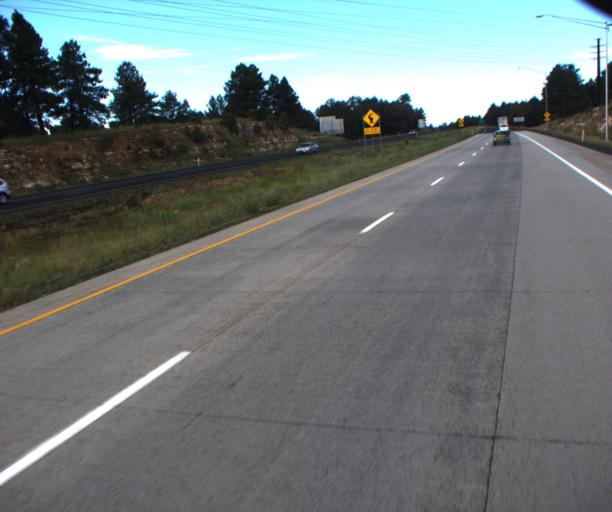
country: US
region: Arizona
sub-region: Coconino County
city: Flagstaff
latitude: 35.1616
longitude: -111.6755
